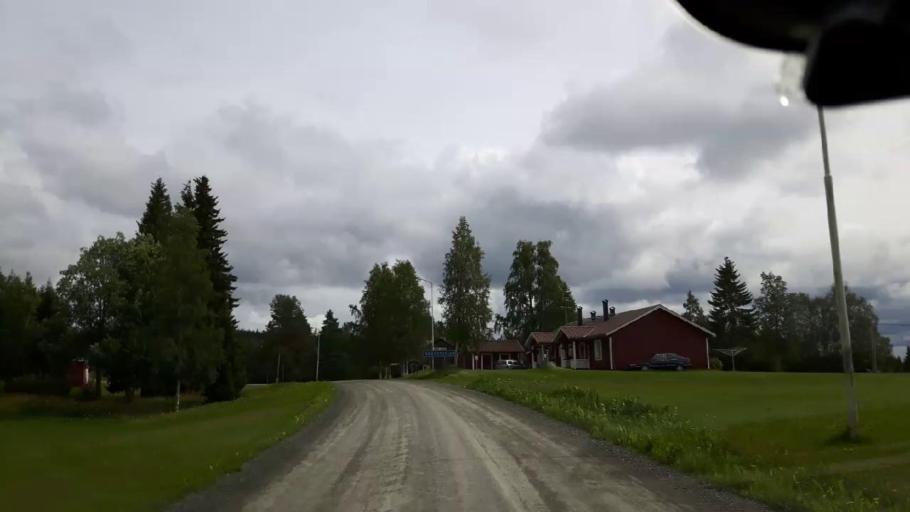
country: SE
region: Jaemtland
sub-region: Krokoms Kommun
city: Valla
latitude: 63.6258
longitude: 14.0329
